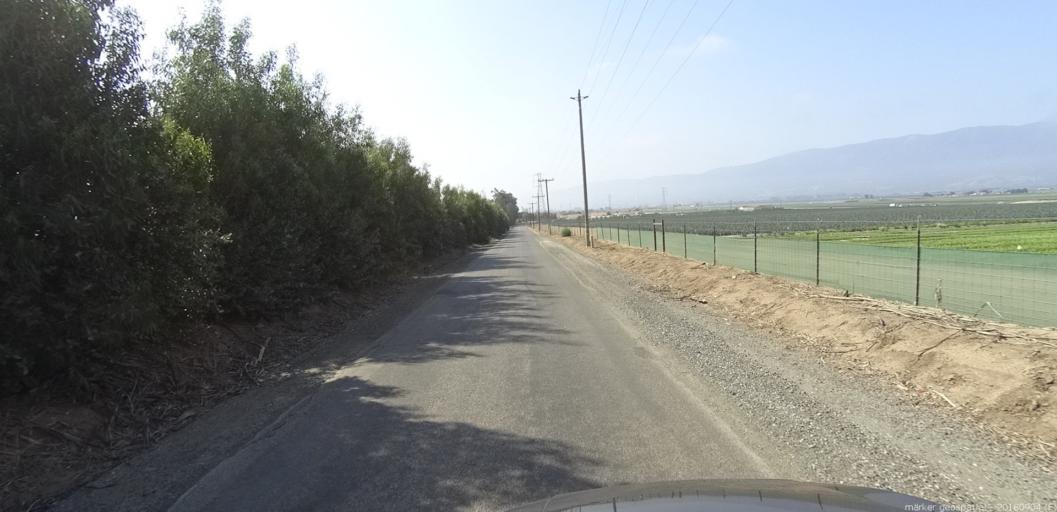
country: US
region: California
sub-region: Monterey County
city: Soledad
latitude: 36.4505
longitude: -121.3318
